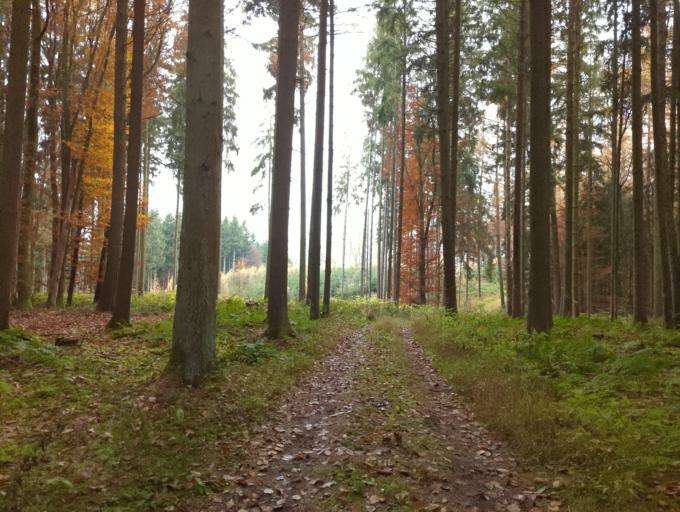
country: DE
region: Bavaria
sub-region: Swabia
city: Wasserburg
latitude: 48.4308
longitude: 10.3072
